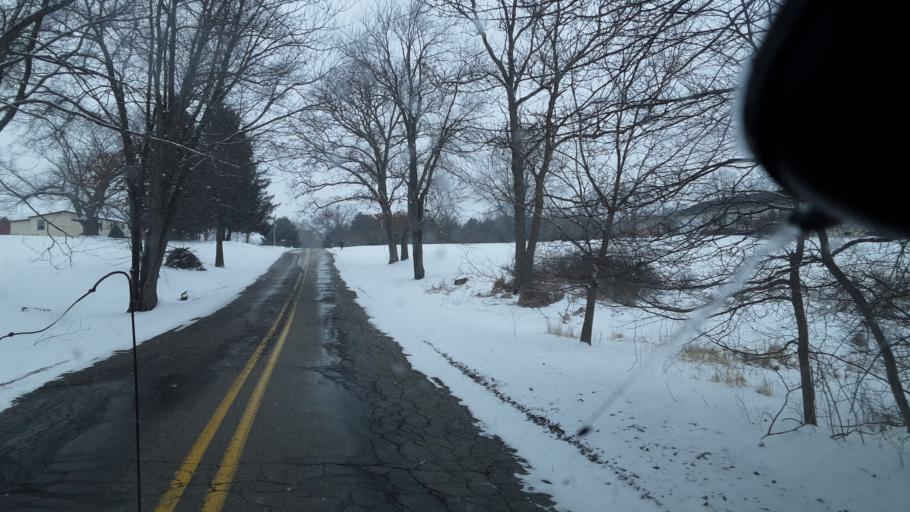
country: US
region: Michigan
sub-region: Ingham County
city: Leslie
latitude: 42.4910
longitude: -84.3801
